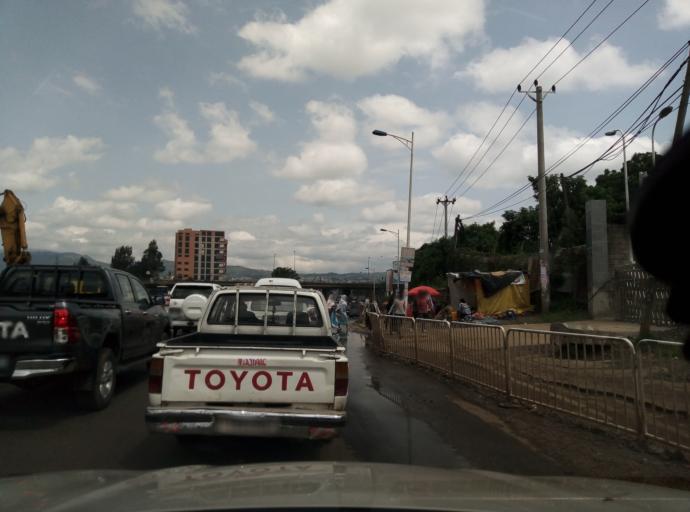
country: ET
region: Adis Abeba
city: Addis Ababa
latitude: 9.0118
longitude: 38.7223
